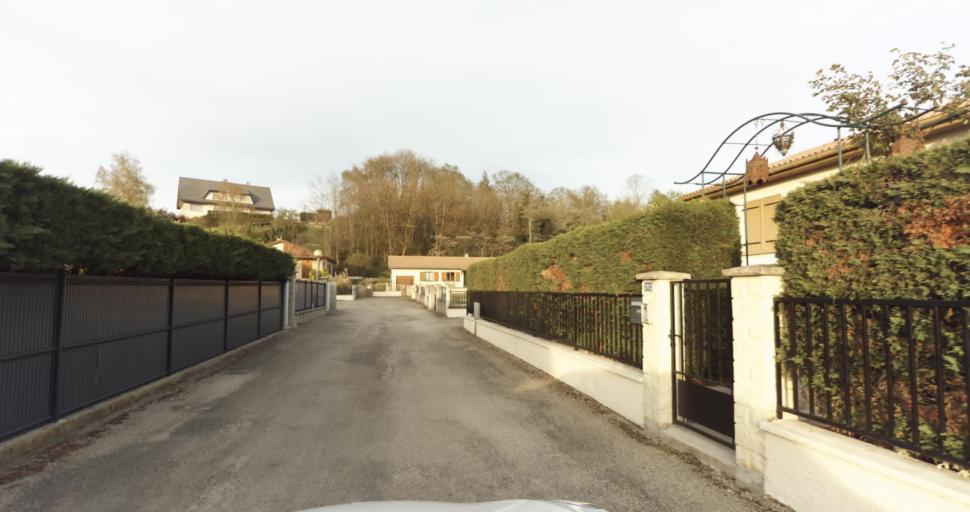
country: FR
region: Rhone-Alpes
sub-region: Departement de l'Ain
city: Amberieu-en-Bugey
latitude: 45.9749
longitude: 5.3522
